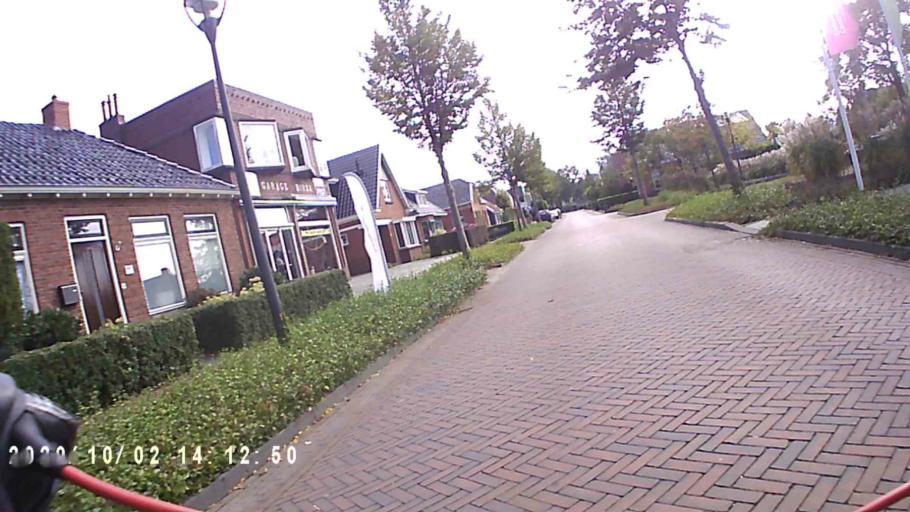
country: NL
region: Groningen
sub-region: Gemeente Zuidhorn
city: Zuidhorn
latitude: 53.2447
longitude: 6.4041
